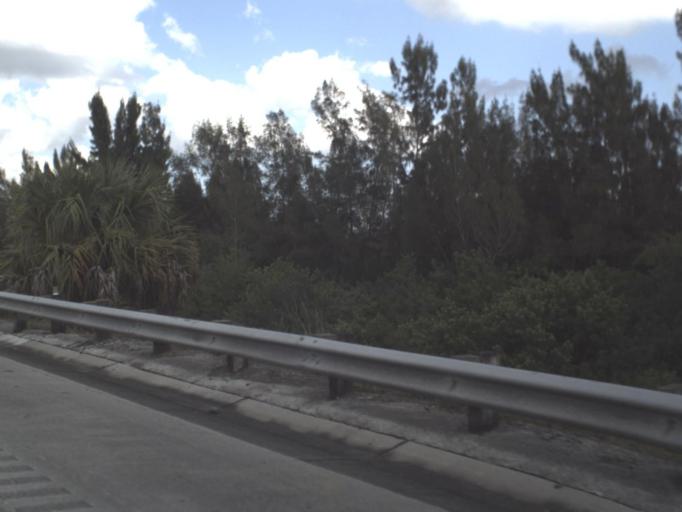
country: US
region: Florida
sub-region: Saint Lucie County
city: Fort Pierce South
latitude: 27.3779
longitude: -80.3856
